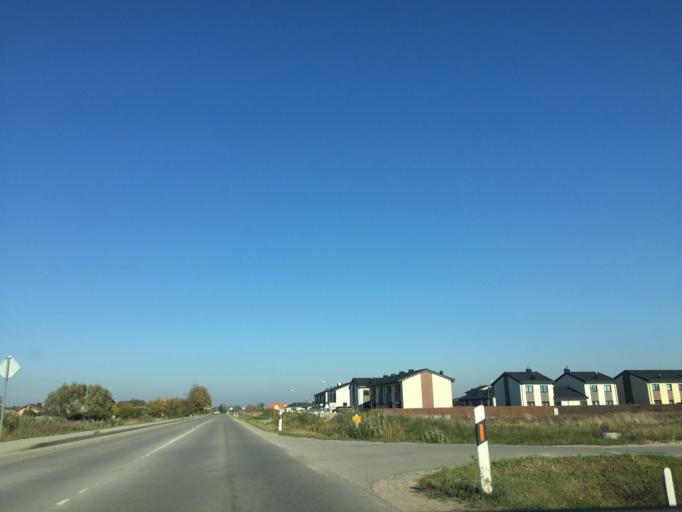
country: LT
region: Klaipedos apskritis
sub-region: Klaipeda
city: Klaipeda
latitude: 55.7393
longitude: 21.1926
